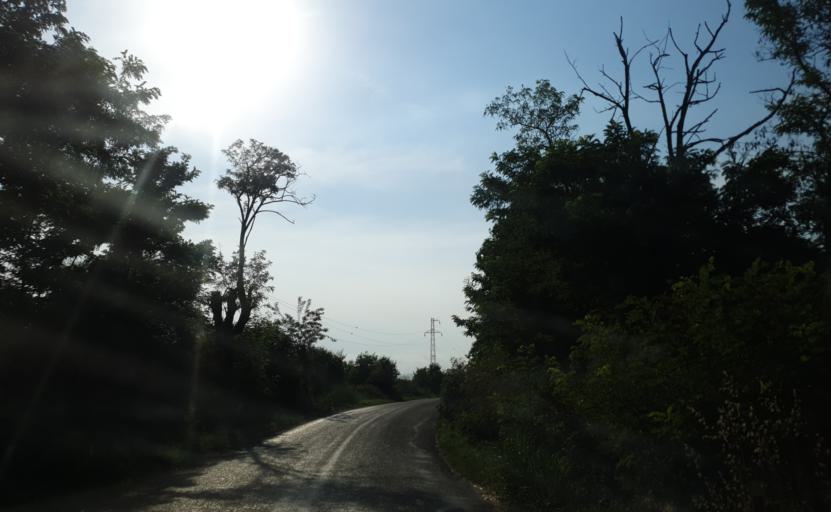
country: TR
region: Tekirdag
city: Muratli
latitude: 41.1939
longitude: 27.4753
